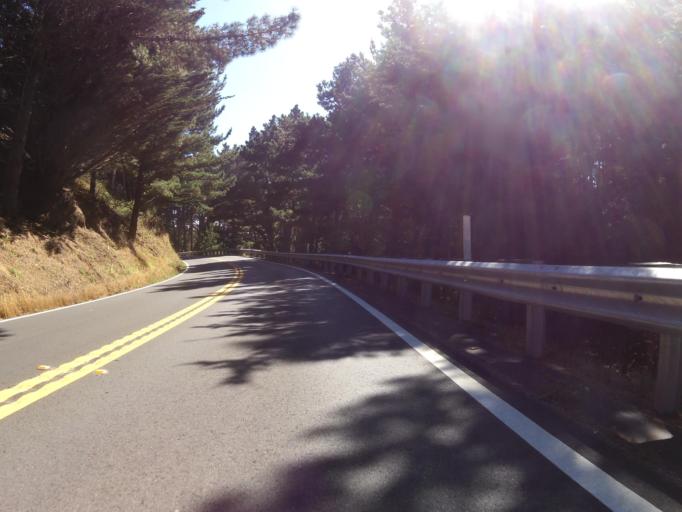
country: US
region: California
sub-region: Mendocino County
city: Fort Bragg
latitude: 39.6017
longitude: -123.7856
